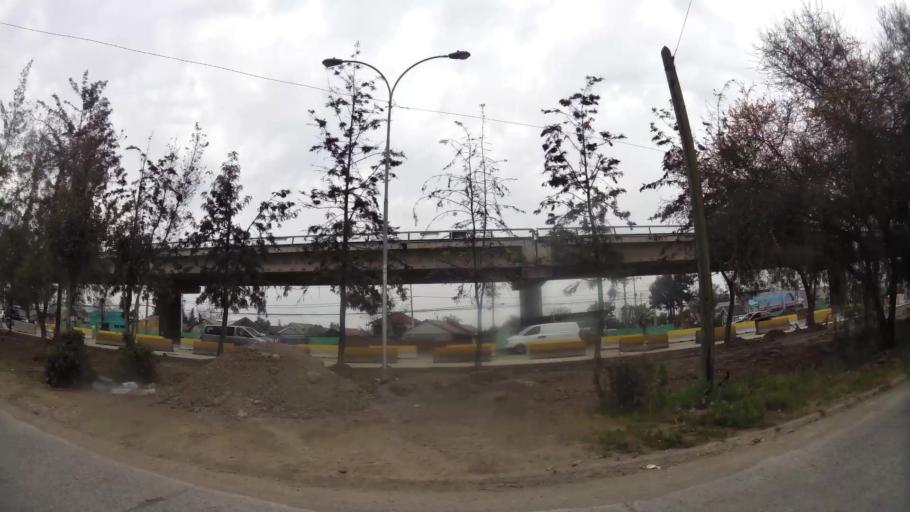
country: CL
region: Santiago Metropolitan
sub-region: Provincia de Santiago
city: Villa Presidente Frei, Nunoa, Santiago, Chile
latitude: -33.5053
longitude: -70.6142
